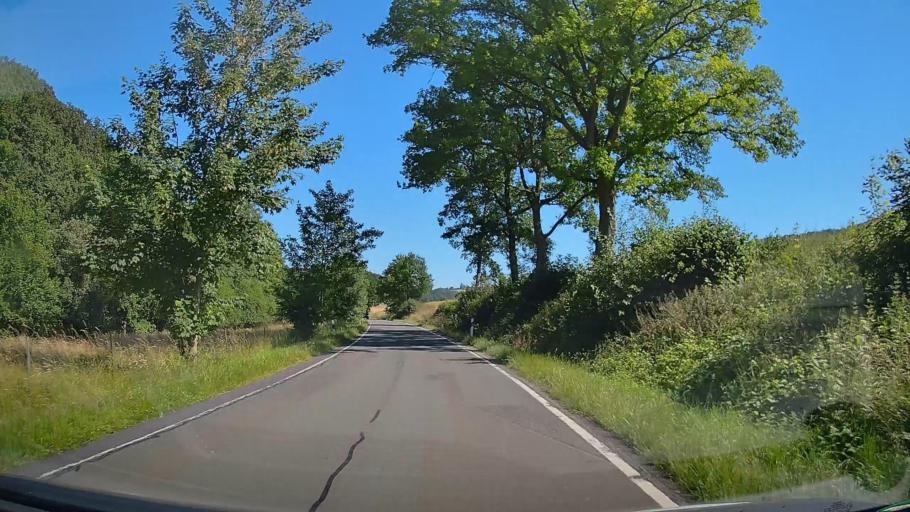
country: DE
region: Lower Saxony
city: Vahlbruch
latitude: 51.9893
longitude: 9.3394
